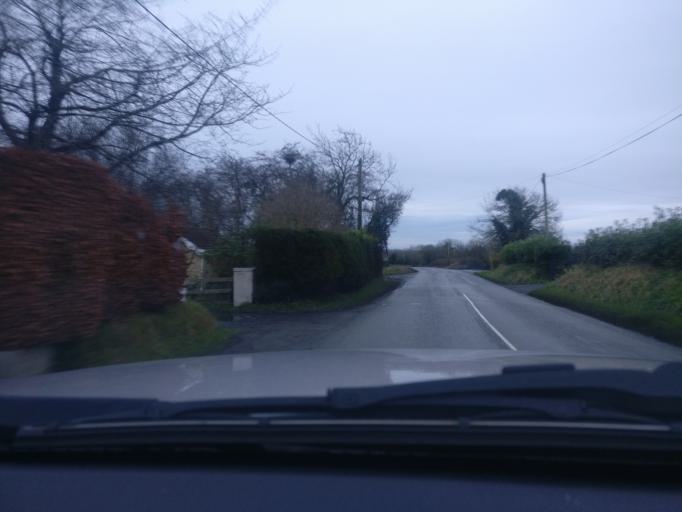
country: IE
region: Leinster
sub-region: Kildare
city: Kilcock
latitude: 53.4562
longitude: -6.6310
